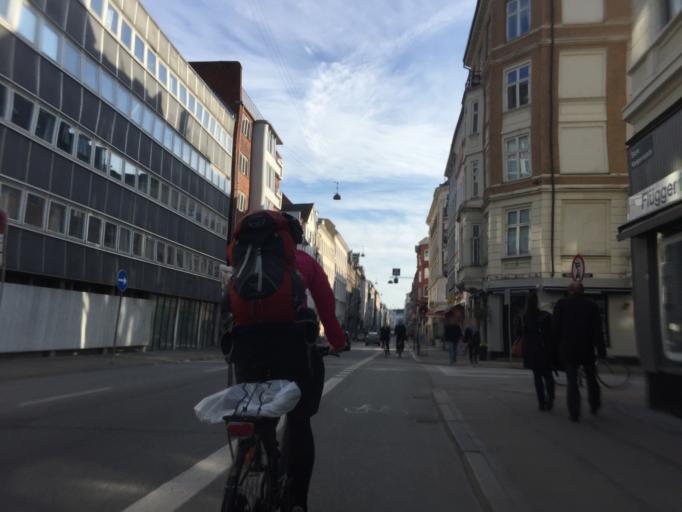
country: DK
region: Capital Region
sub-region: Kobenhavn
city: Christianshavn
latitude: 55.6867
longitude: 12.5897
